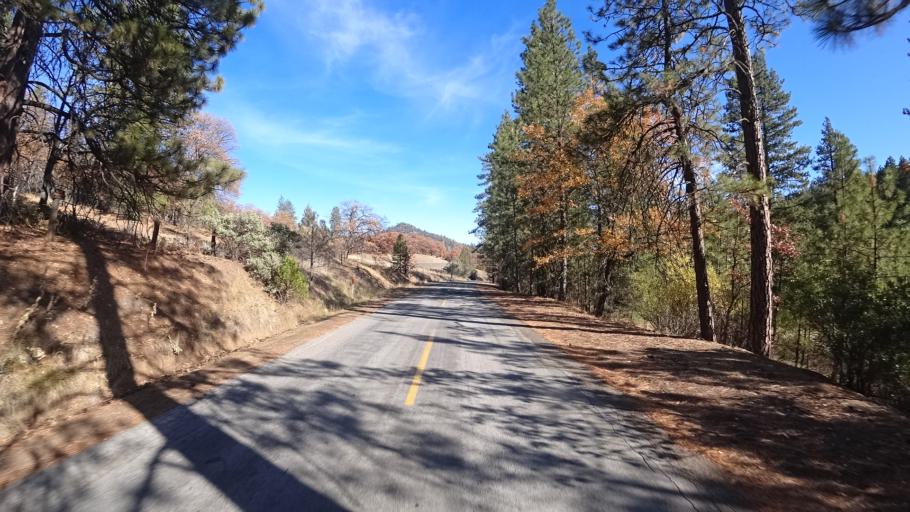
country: US
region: California
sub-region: Siskiyou County
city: Yreka
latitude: 41.7227
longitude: -122.6969
